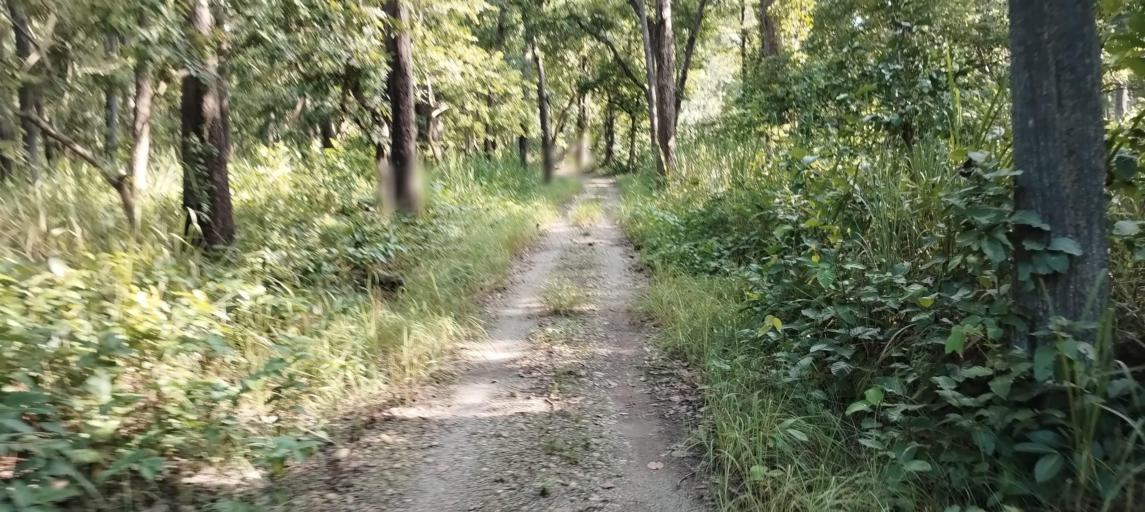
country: NP
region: Far Western
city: Tikapur
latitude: 28.5323
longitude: 81.2833
